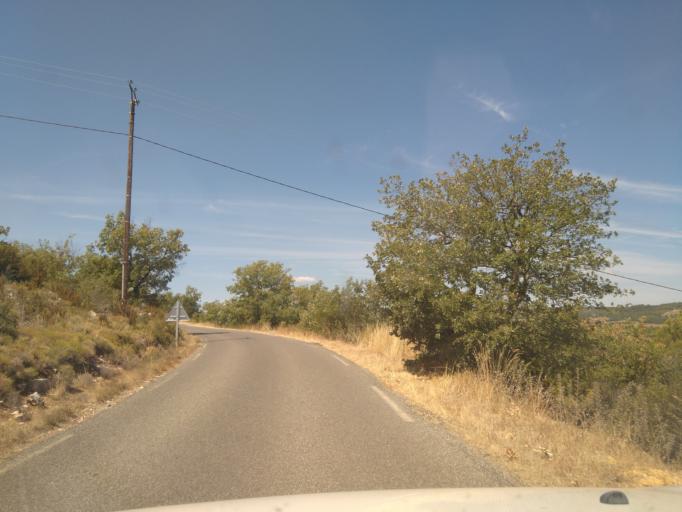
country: FR
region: Provence-Alpes-Cote d'Azur
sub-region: Departement du Var
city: Regusse
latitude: 43.7123
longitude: 6.0890
